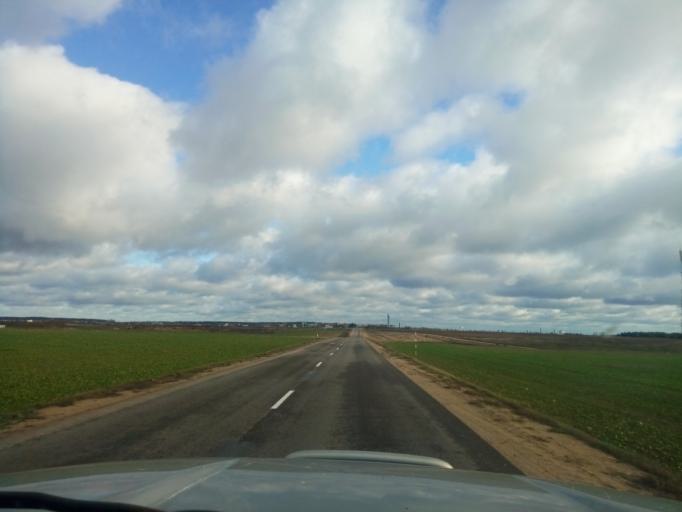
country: BY
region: Minsk
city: Kapyl'
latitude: 53.1479
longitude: 27.0541
